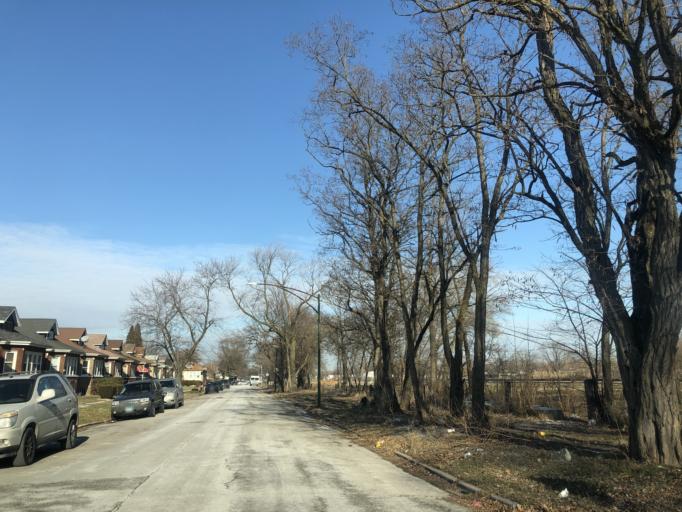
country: US
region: Illinois
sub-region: Cook County
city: Evergreen Park
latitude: 41.7612
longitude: -87.6794
